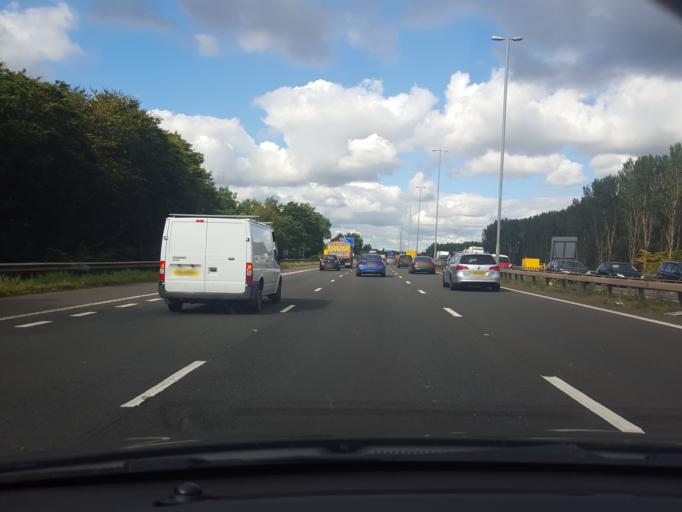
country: GB
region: Scotland
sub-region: South Lanarkshire
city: Hamilton
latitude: 55.7926
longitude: -4.0412
